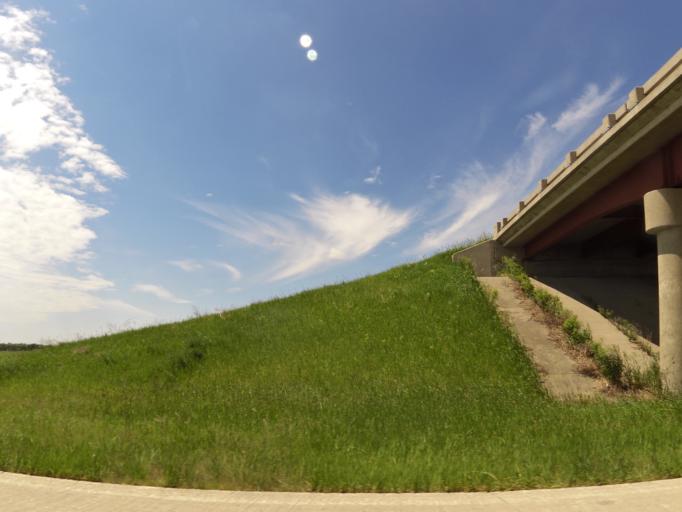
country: US
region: North Dakota
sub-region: Walsh County
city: Grafton
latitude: 48.3243
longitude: -97.1897
